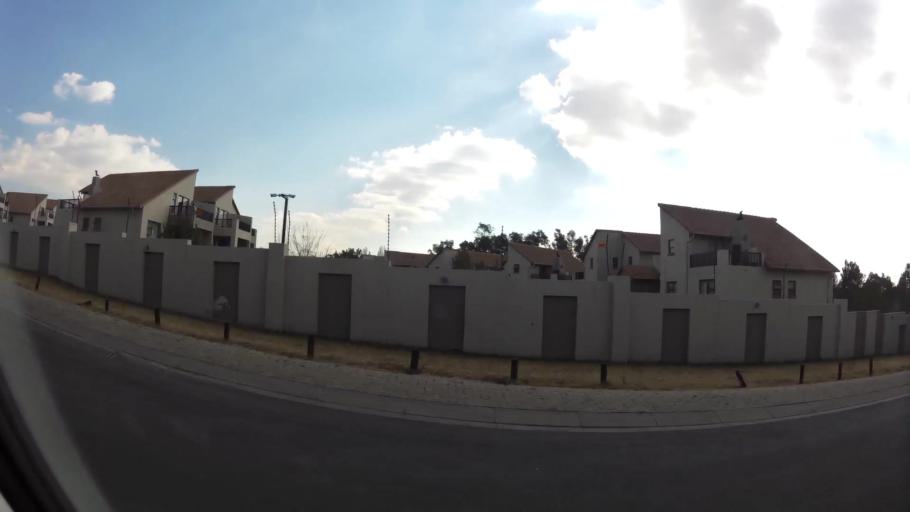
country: ZA
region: Gauteng
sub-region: City of Johannesburg Metropolitan Municipality
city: Diepsloot
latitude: -26.0233
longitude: 28.0359
